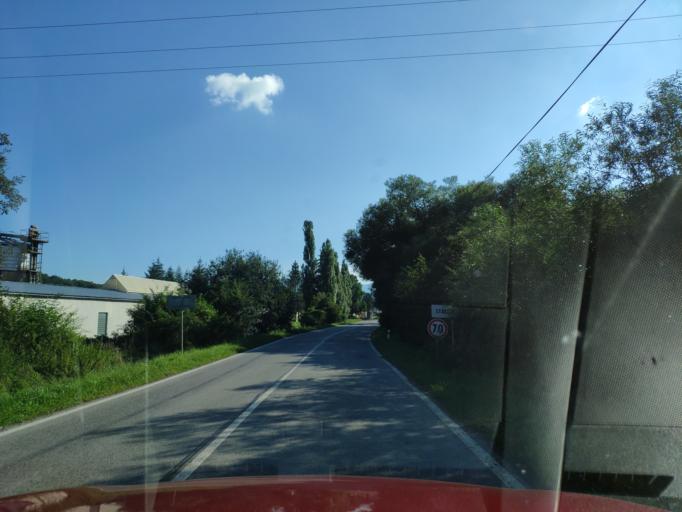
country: SK
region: Presovsky
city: Snina
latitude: 49.0156
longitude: 22.2477
